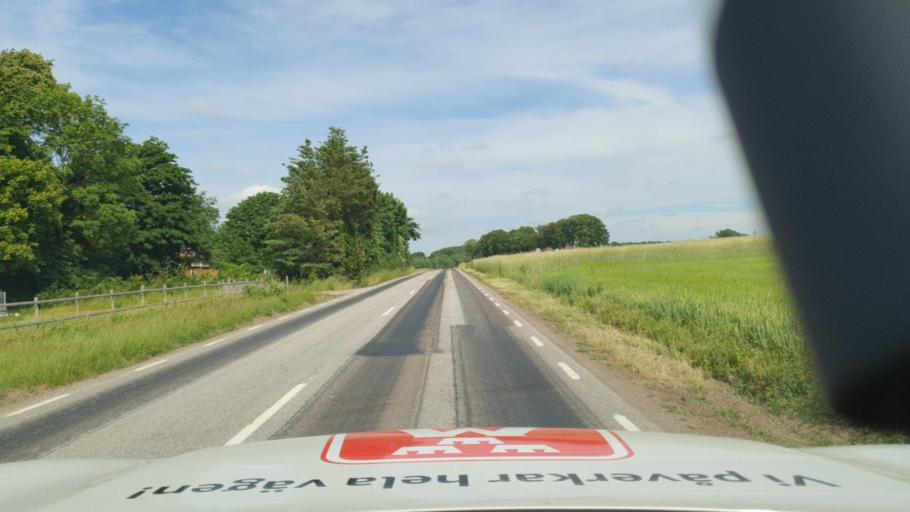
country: SE
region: Skane
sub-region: Sjobo Kommun
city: Sjoebo
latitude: 55.7243
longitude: 13.8075
